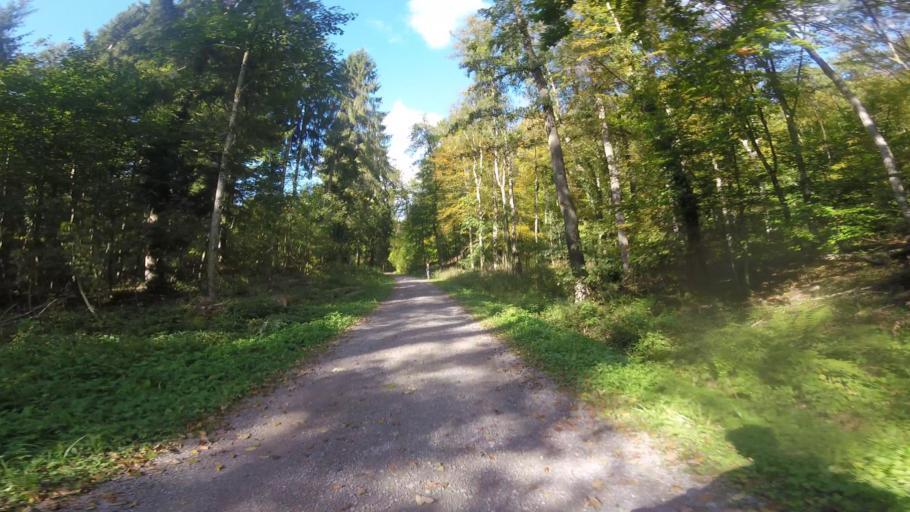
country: DE
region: Baden-Wuerttemberg
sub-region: Regierungsbezirk Stuttgart
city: Grossbottwar
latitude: 48.9888
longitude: 9.3288
